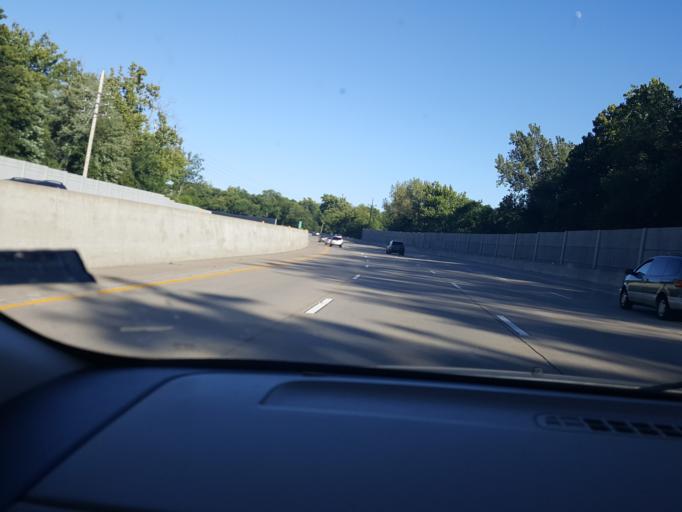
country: US
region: Missouri
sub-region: Saint Louis County
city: Ladue
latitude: 38.6328
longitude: -90.3875
